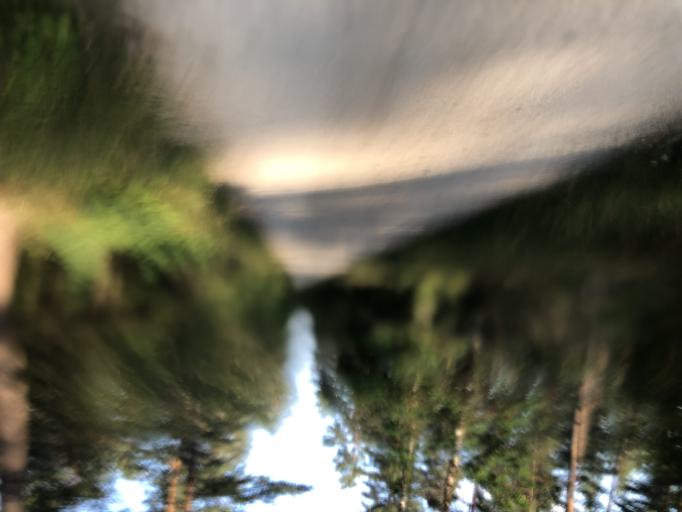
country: DE
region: Bavaria
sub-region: Regierungsbezirk Mittelfranken
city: Uttenreuth
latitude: 49.5689
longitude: 11.0912
